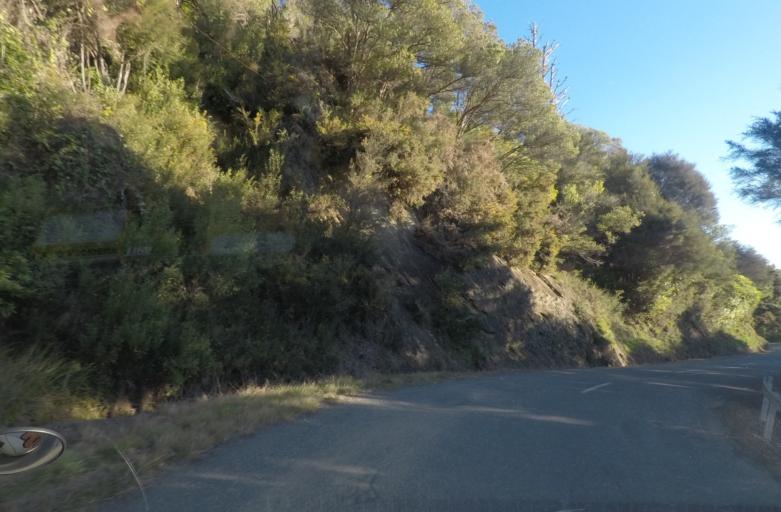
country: NZ
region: Marlborough
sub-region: Marlborough District
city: Picton
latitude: -41.2687
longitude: 173.9553
